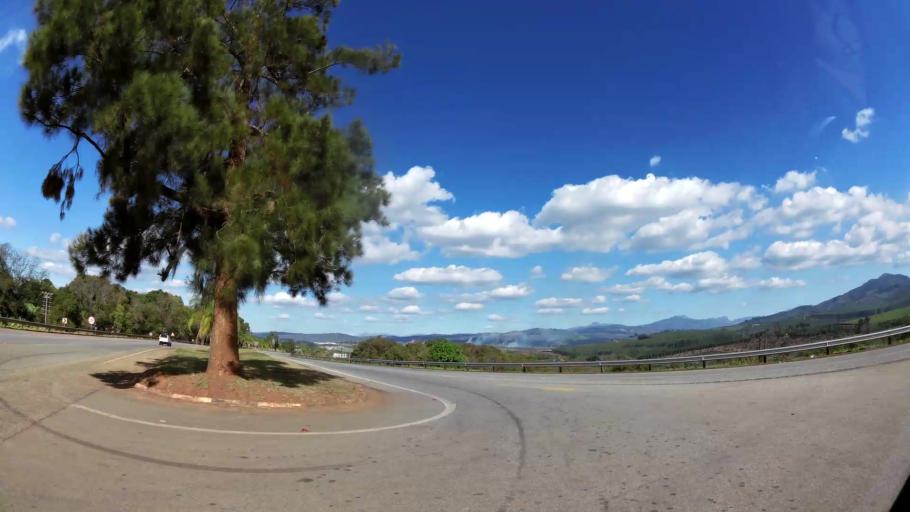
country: ZA
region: Limpopo
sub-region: Mopani District Municipality
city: Tzaneen
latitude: -23.8029
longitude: 30.1267
